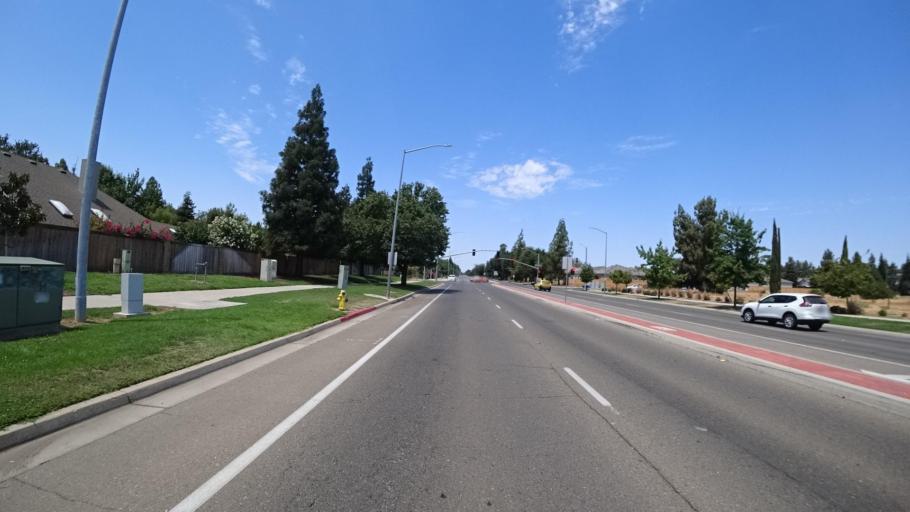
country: US
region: California
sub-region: Fresno County
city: Tarpey Village
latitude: 36.7938
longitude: -119.6722
